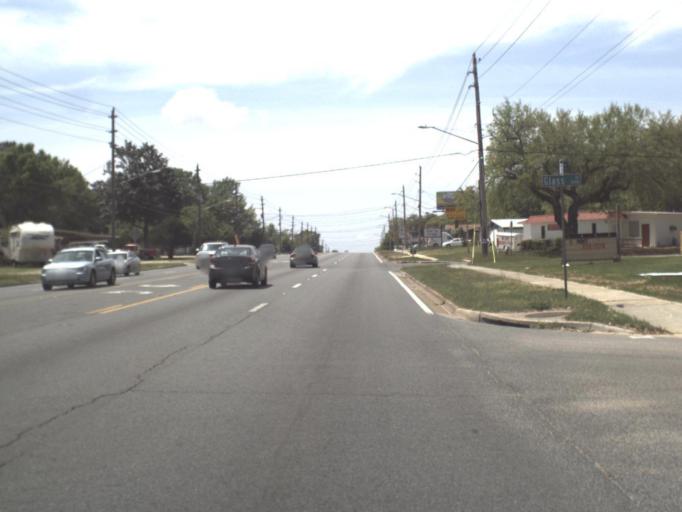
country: US
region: Florida
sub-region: Escambia County
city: Brent
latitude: 30.4631
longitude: -87.2638
